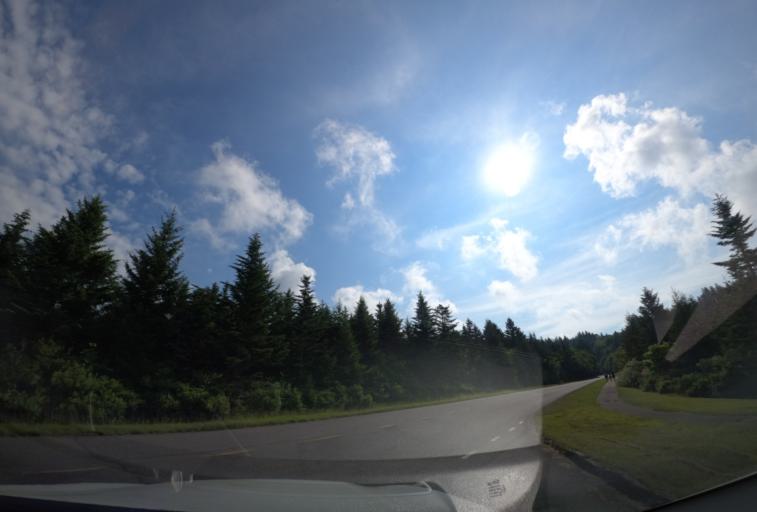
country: US
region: North Carolina
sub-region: Transylvania County
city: Brevard
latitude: 35.3054
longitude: -82.8992
